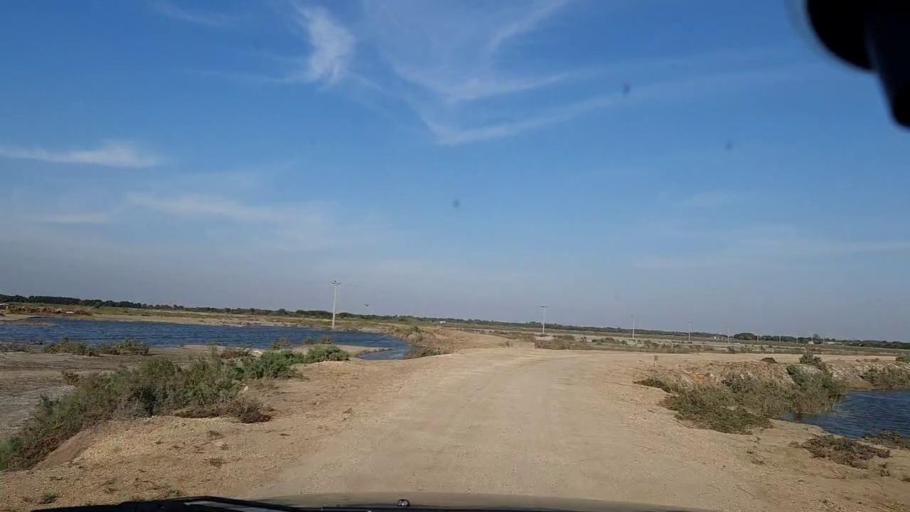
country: PK
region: Sindh
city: Mirpur Batoro
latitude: 24.6314
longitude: 68.2941
